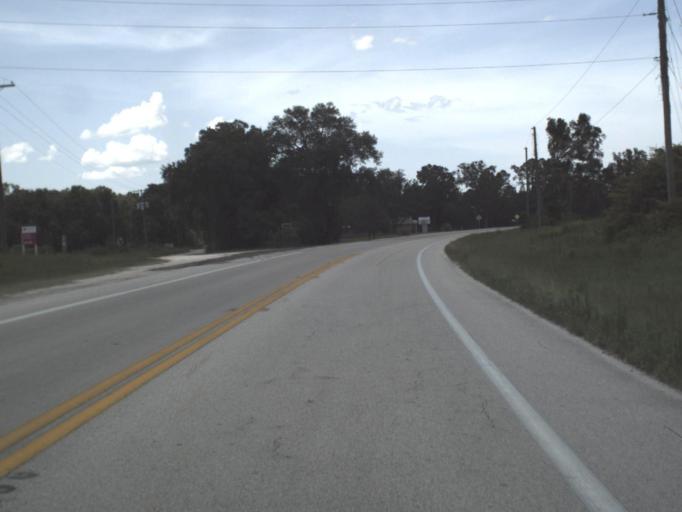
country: US
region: Florida
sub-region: Gilchrist County
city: Trenton
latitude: 29.5960
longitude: -82.8232
